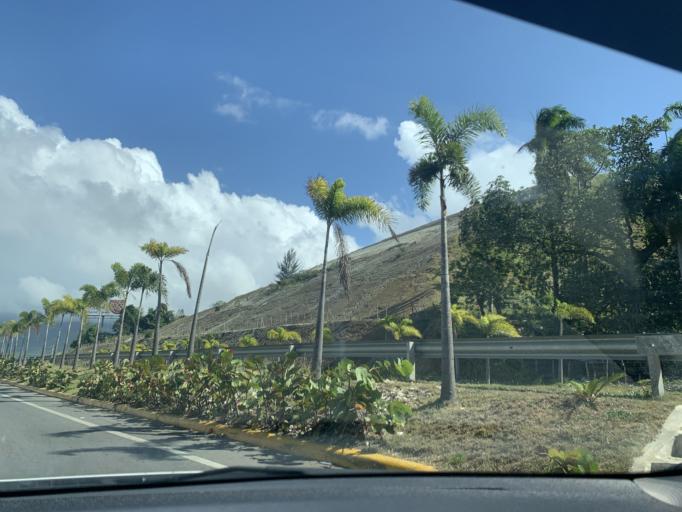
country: DO
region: Puerto Plata
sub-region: Puerto Plata
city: Puerto Plata
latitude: 19.8173
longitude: -70.7332
